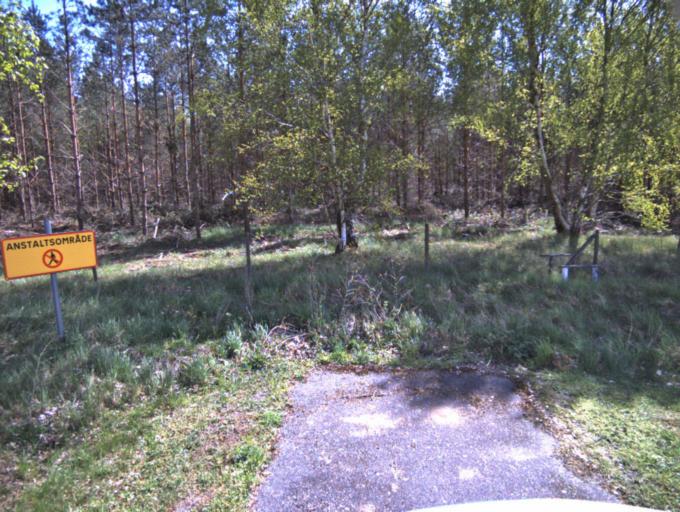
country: SE
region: Skane
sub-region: Kristianstads Kommun
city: Norra Asum
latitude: 55.9818
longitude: 14.0824
